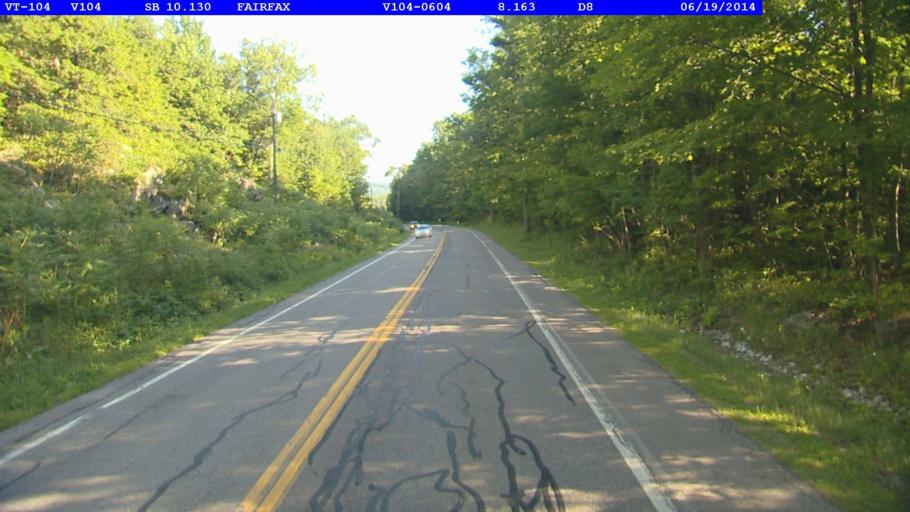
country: US
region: Vermont
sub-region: Chittenden County
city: Milton
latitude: 44.7021
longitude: -73.0370
